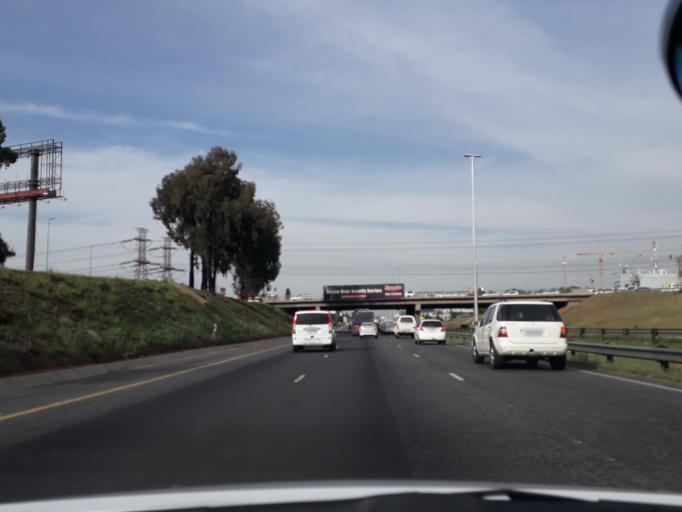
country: ZA
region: Gauteng
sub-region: City of Johannesburg Metropolitan Municipality
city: Modderfontein
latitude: -26.1387
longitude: 28.1940
